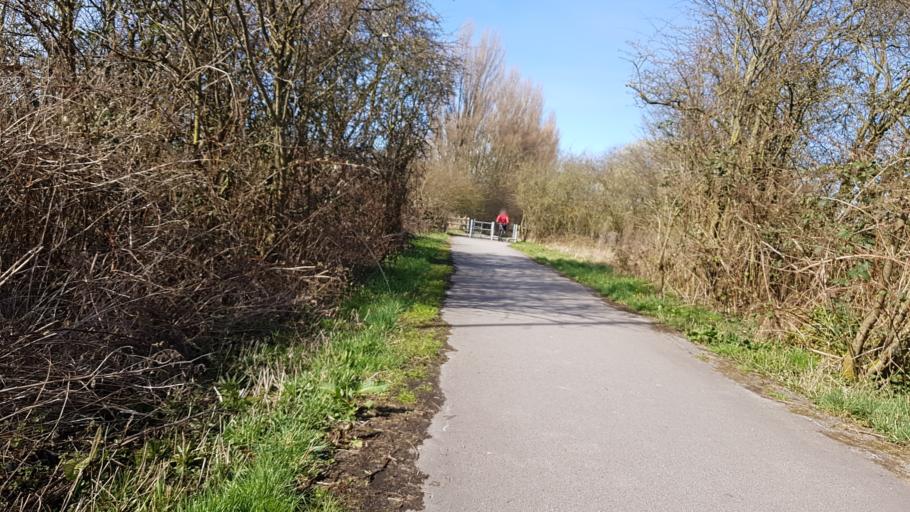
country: GB
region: England
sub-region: City of York
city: York
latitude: 53.9793
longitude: -1.0811
